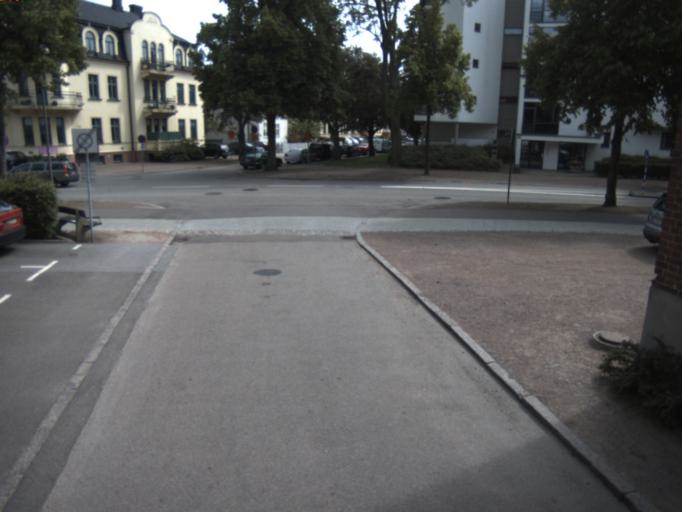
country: SE
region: Skane
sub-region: Helsingborg
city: Helsingborg
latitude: 56.0503
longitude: 12.7030
